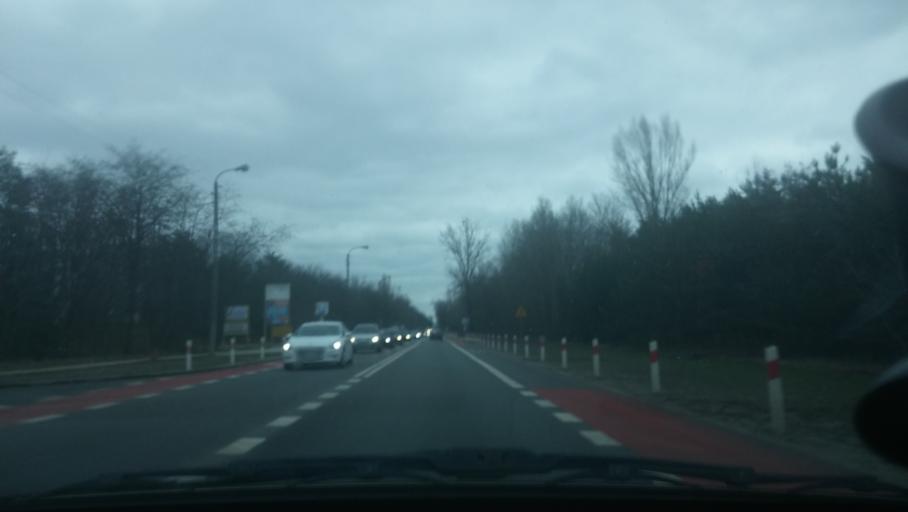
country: PL
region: Masovian Voivodeship
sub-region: Warszawa
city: Bialoleka
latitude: 52.3100
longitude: 21.0044
